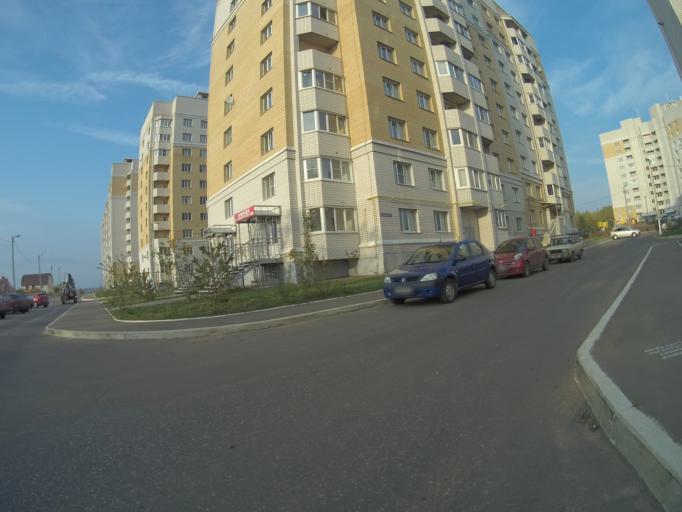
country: RU
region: Vladimir
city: Vladimir
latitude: 56.1603
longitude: 40.3729
